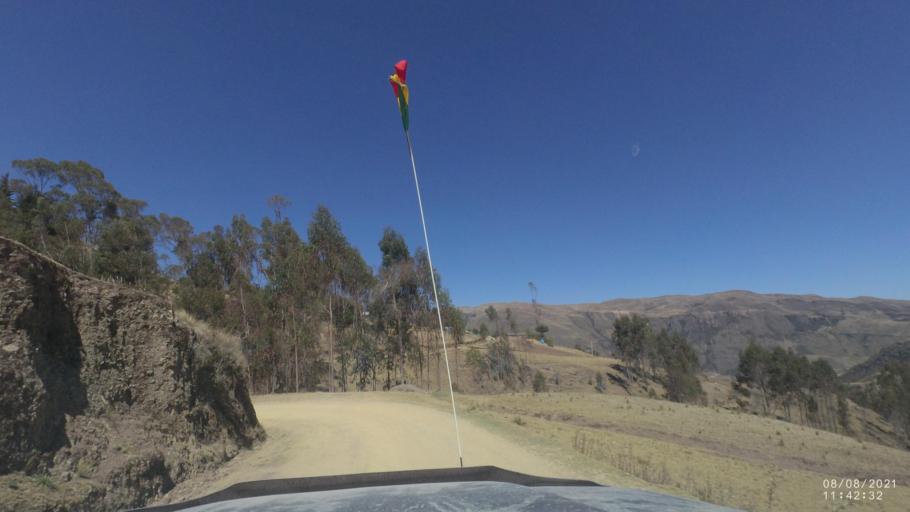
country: BO
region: Cochabamba
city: Colchani
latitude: -16.7975
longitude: -66.6400
